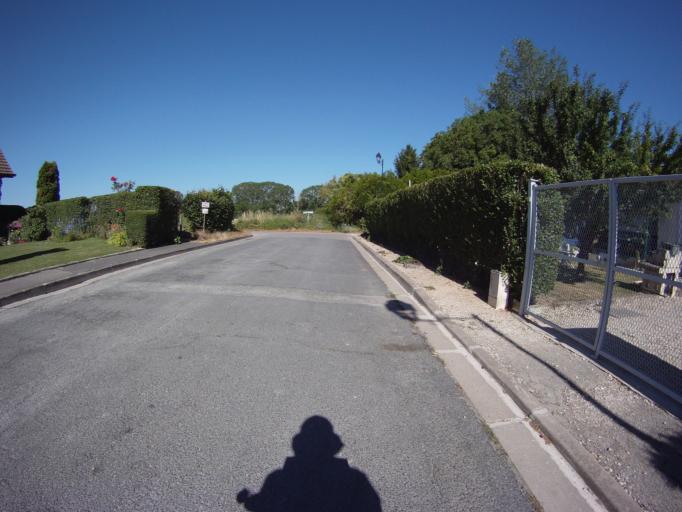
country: FR
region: Champagne-Ardenne
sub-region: Departement de la Marne
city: Ay
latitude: 49.0523
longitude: 3.9973
